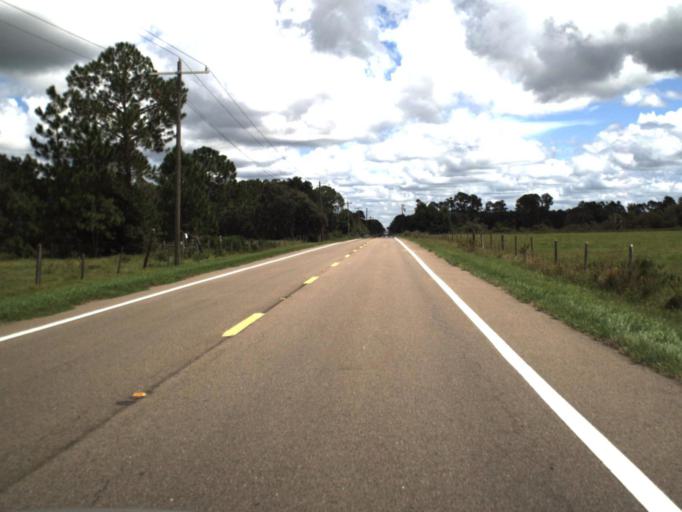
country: US
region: Florida
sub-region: Polk County
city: Frostproof
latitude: 27.7335
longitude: -81.6304
